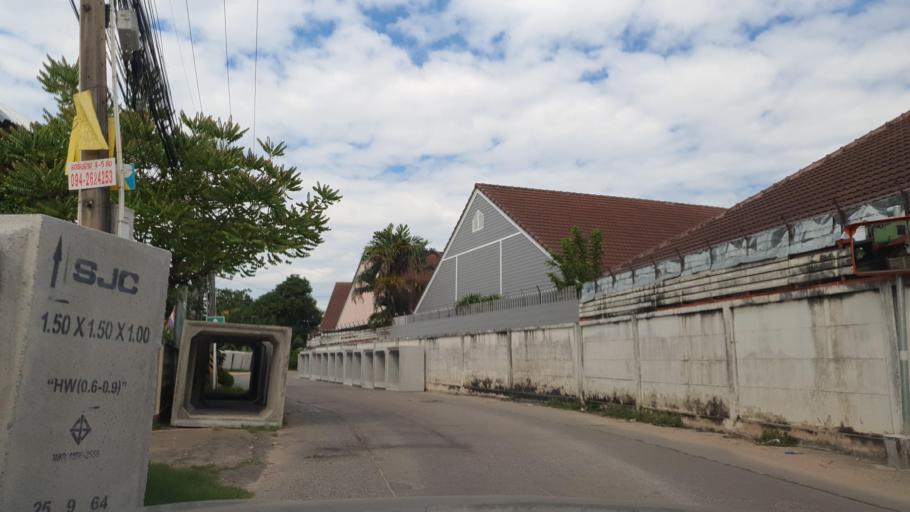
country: TH
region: Chon Buri
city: Phatthaya
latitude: 12.9571
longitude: 100.9231
